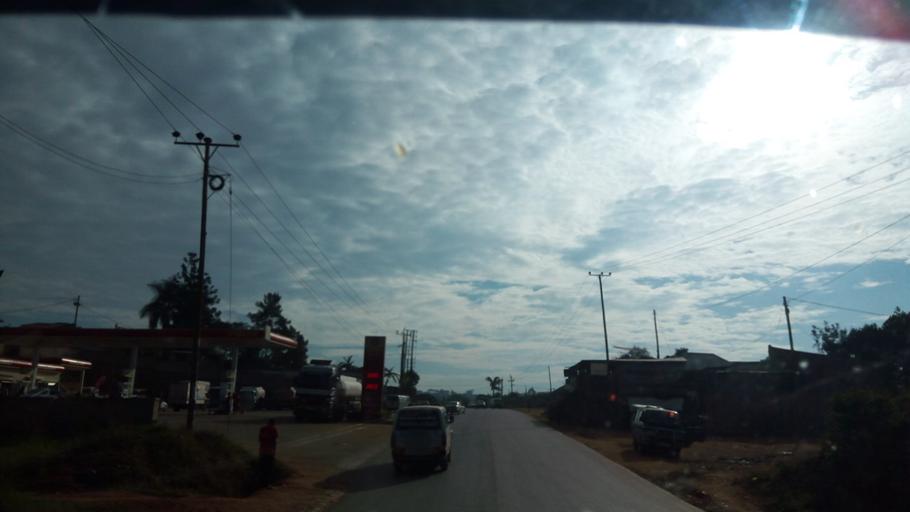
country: UG
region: Central Region
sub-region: Wakiso District
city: Wakiso
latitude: 0.4487
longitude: 32.5312
